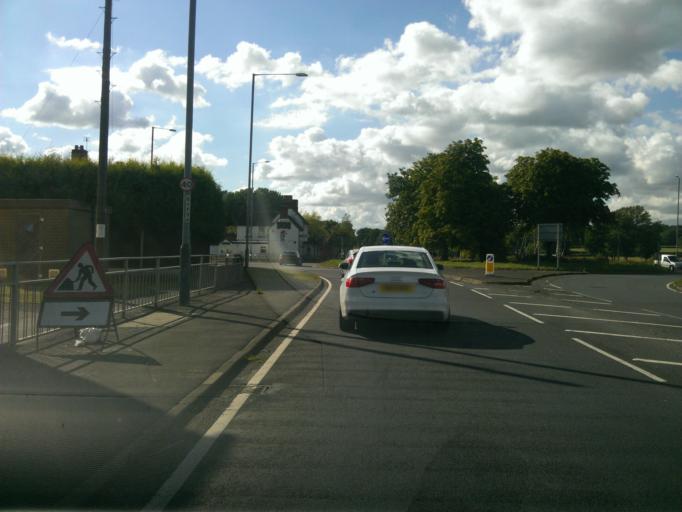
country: GB
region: England
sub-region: Warwickshire
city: Atherstone
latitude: 52.5919
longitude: -1.5954
